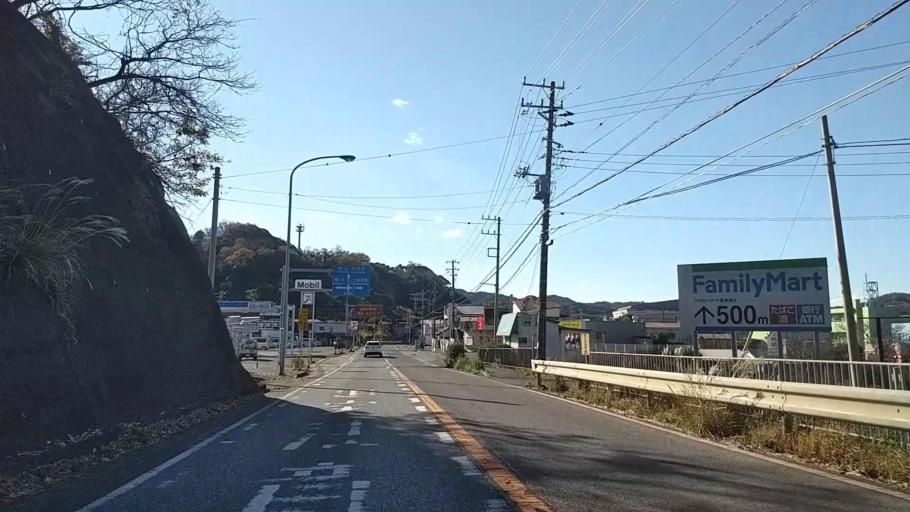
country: JP
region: Chiba
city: Futtsu
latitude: 35.2248
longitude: 139.8738
